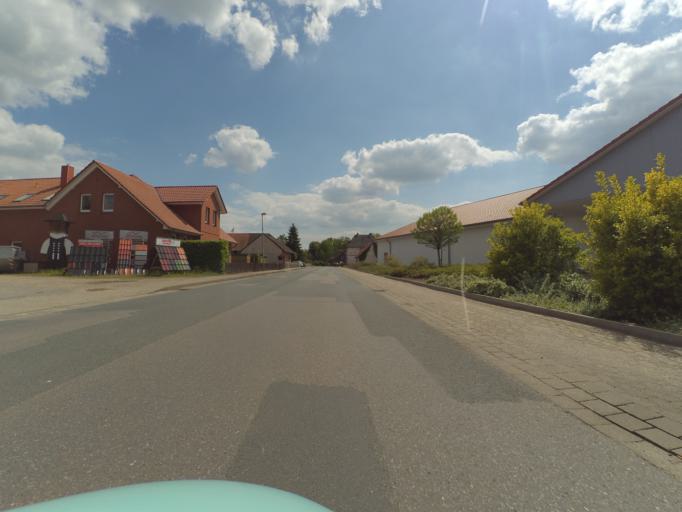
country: DE
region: Lower Saxony
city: Muden
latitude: 52.5226
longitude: 10.3680
